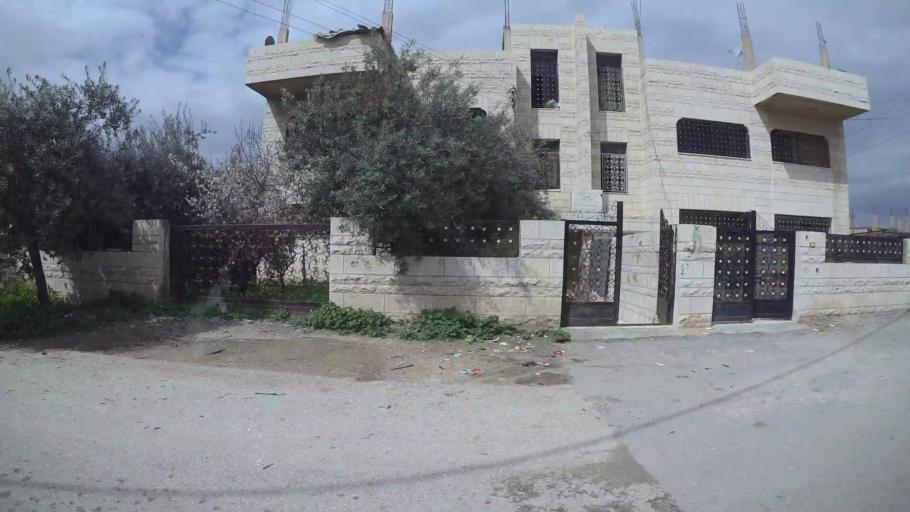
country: JO
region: Amman
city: Al Jubayhah
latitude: 32.0545
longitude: 35.8254
